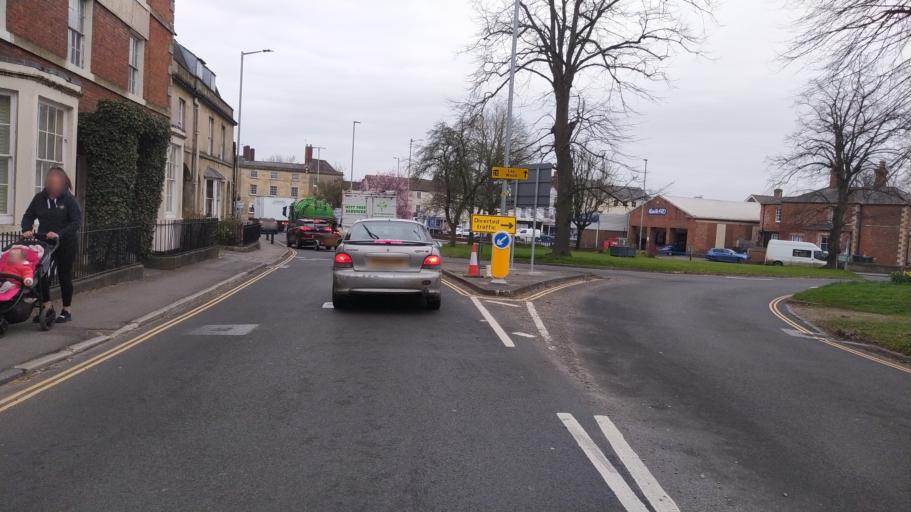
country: GB
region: England
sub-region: Wiltshire
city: Devizes
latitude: 51.3512
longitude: -1.9897
